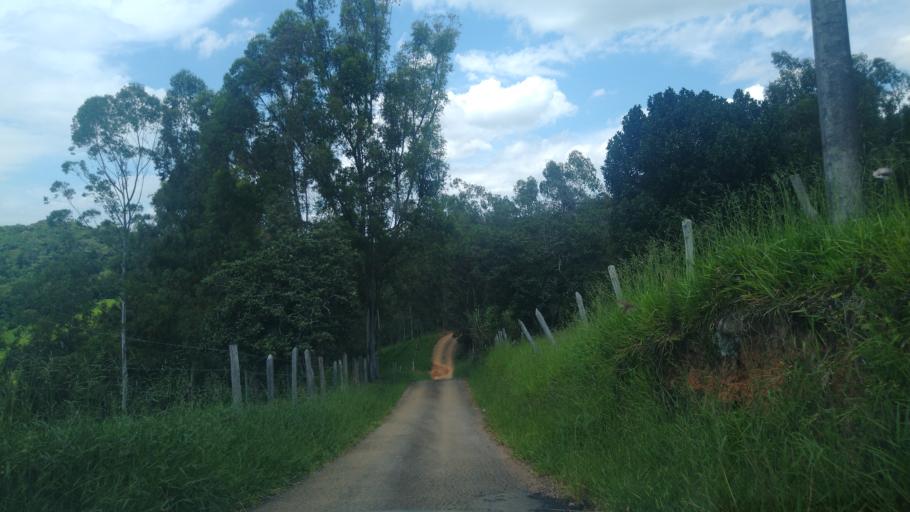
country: BR
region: Minas Gerais
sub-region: Extrema
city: Extrema
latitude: -22.7509
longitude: -46.2969
